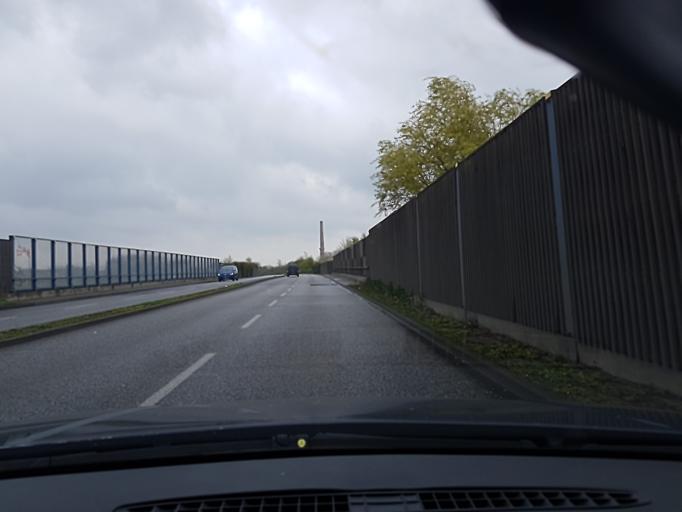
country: DE
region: Berlin
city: Adlershof
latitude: 52.4426
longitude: 13.5593
